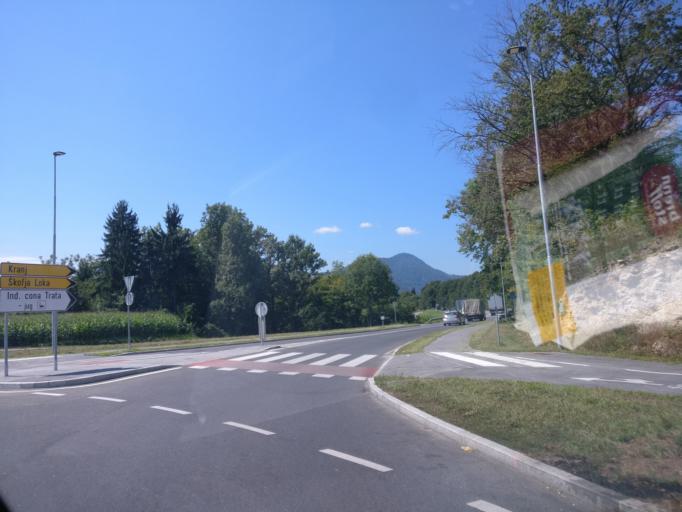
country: SI
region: Skofja Loka
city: Sv. Duh
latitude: 46.1691
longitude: 14.3458
